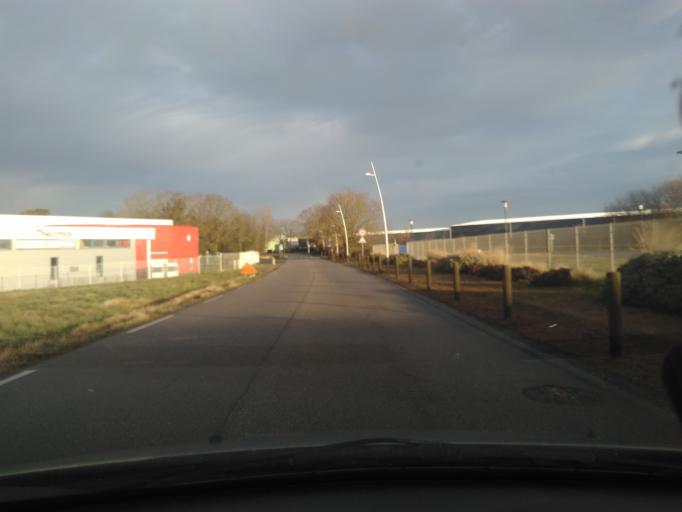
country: FR
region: Pays de la Loire
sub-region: Departement de la Vendee
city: Dompierre-sur-Yon
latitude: 46.6973
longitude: -1.3722
